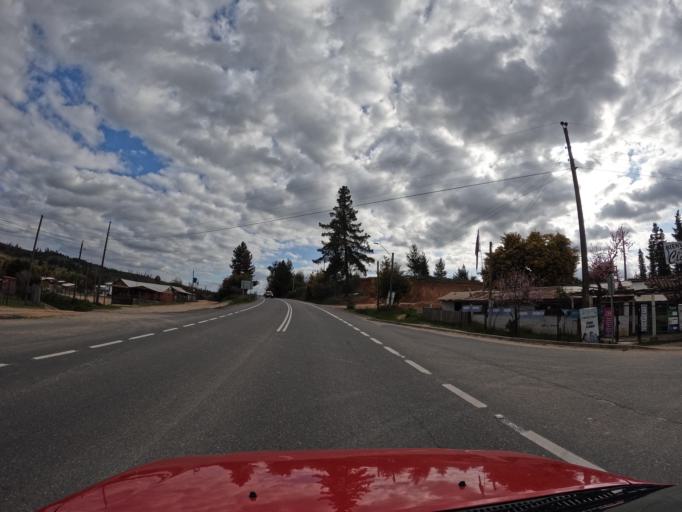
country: CL
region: Maule
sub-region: Provincia de Linares
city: San Javier
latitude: -35.5584
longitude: -72.0892
